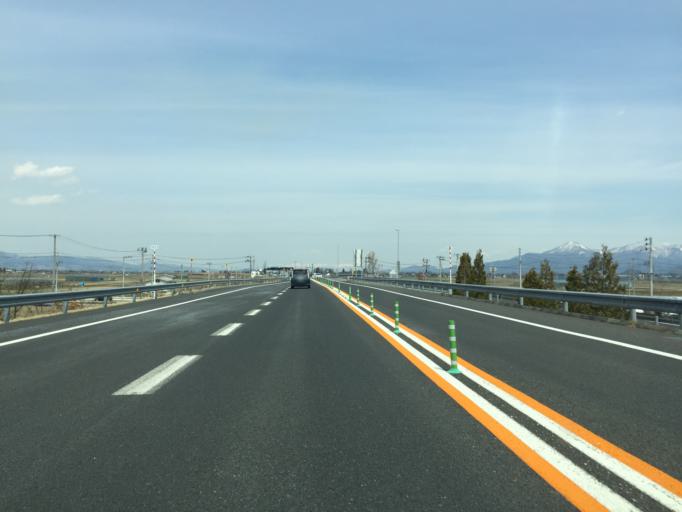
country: JP
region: Yamagata
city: Tendo
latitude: 38.3654
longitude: 140.3463
